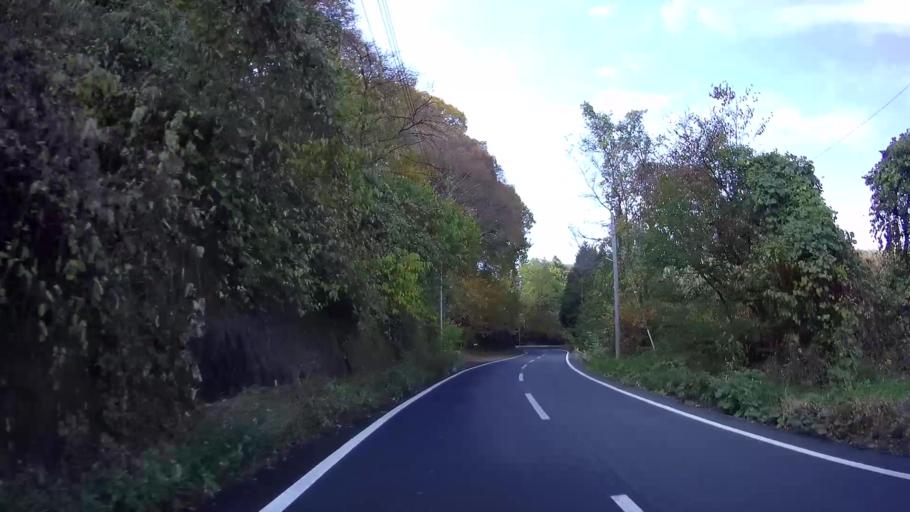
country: JP
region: Gunma
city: Nakanojomachi
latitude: 36.5054
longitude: 138.7323
